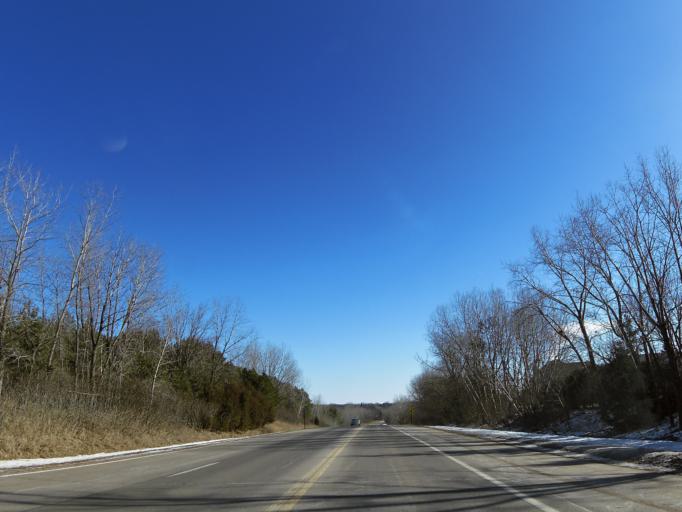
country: US
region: Minnesota
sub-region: Washington County
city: Stillwater
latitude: 45.0579
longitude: -92.8389
